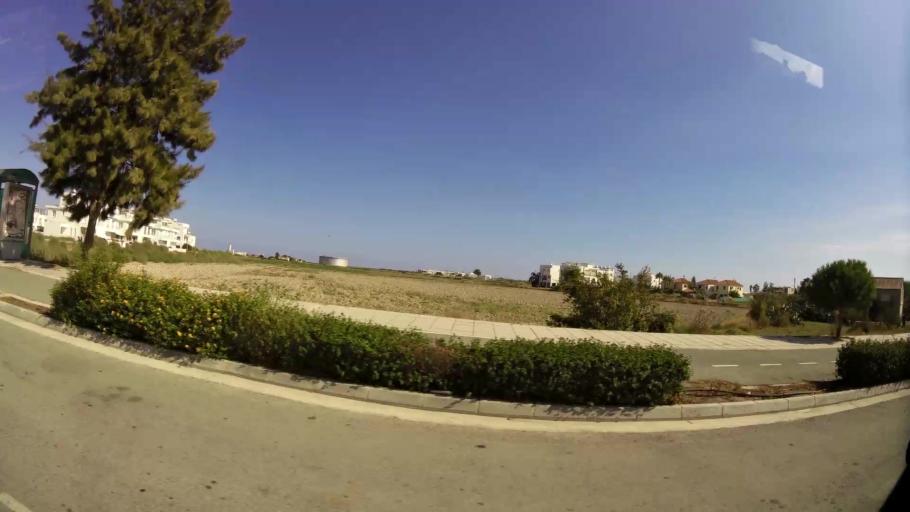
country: CY
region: Larnaka
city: Livadia
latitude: 34.9467
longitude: 33.6350
